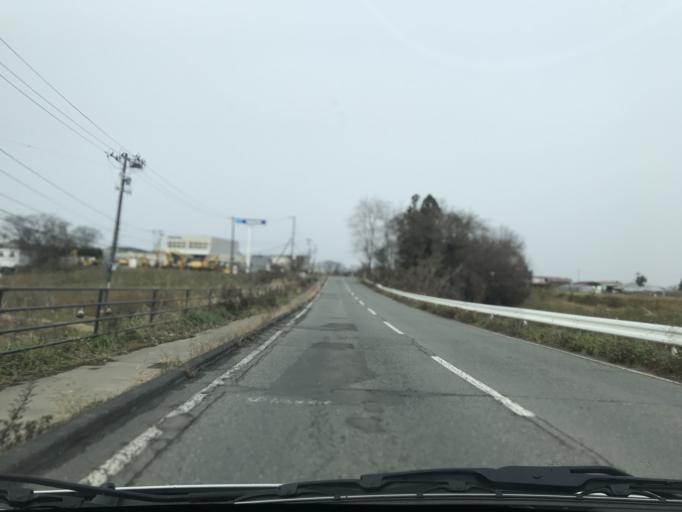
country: JP
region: Iwate
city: Mizusawa
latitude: 39.1716
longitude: 141.1411
